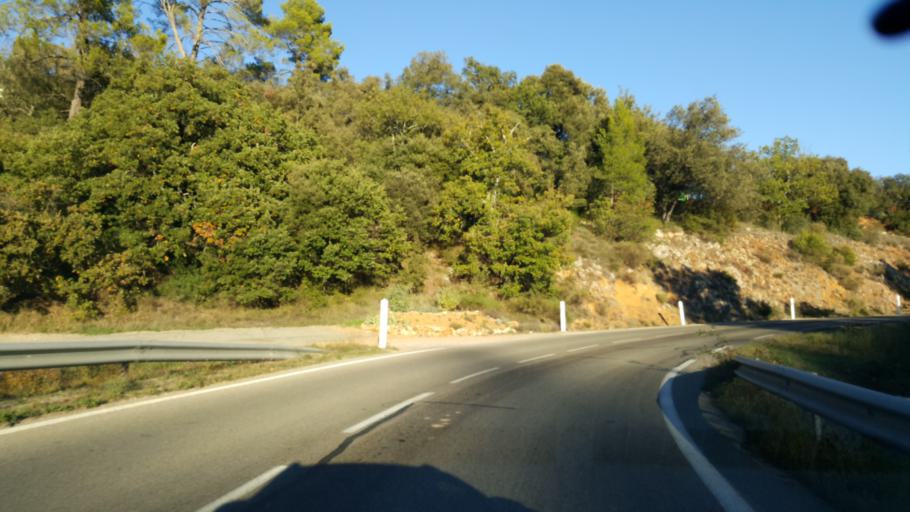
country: FR
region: Provence-Alpes-Cote d'Azur
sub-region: Departement du Var
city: Barjols
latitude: 43.5764
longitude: 5.9553
